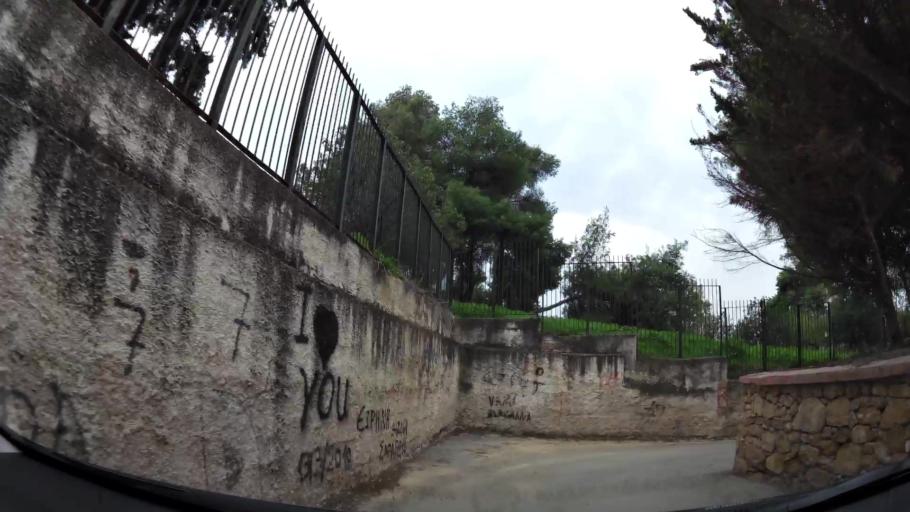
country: GR
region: Attica
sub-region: Nomarchia Athinas
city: Marousi
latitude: 38.0448
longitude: 23.7827
